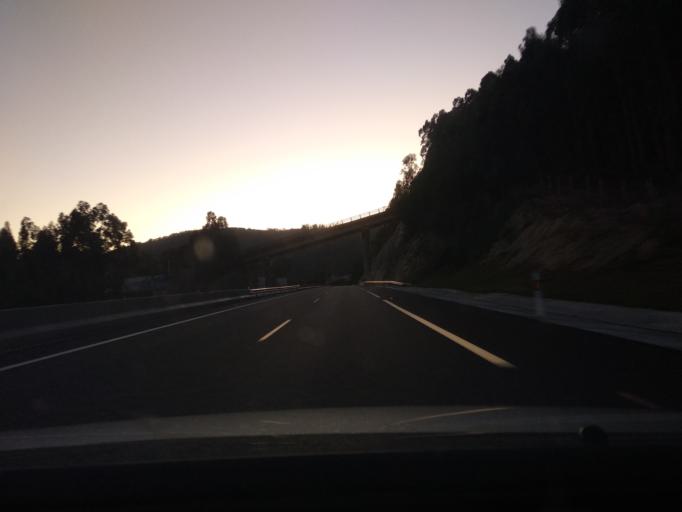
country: ES
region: Galicia
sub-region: Provincia de Pontevedra
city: Moana
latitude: 42.3091
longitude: -8.7295
